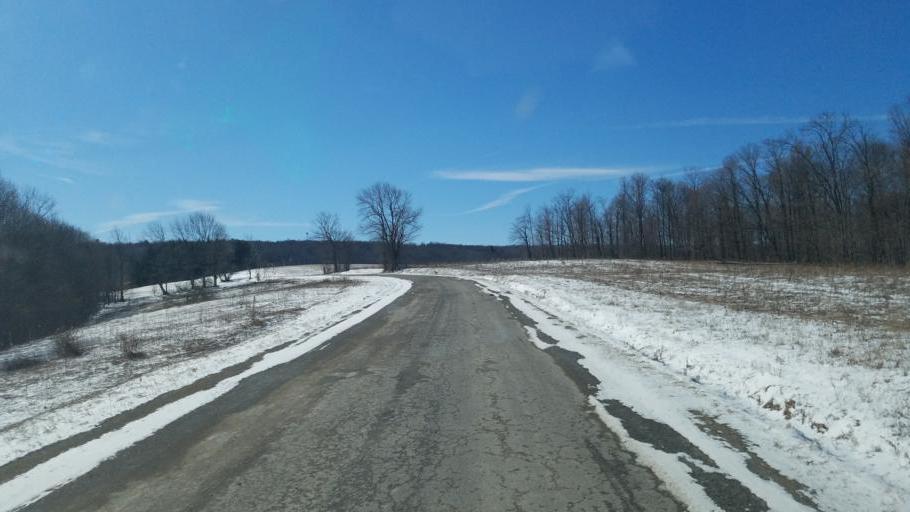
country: US
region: New York
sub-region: Allegany County
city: Wellsville
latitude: 42.0656
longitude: -78.0116
